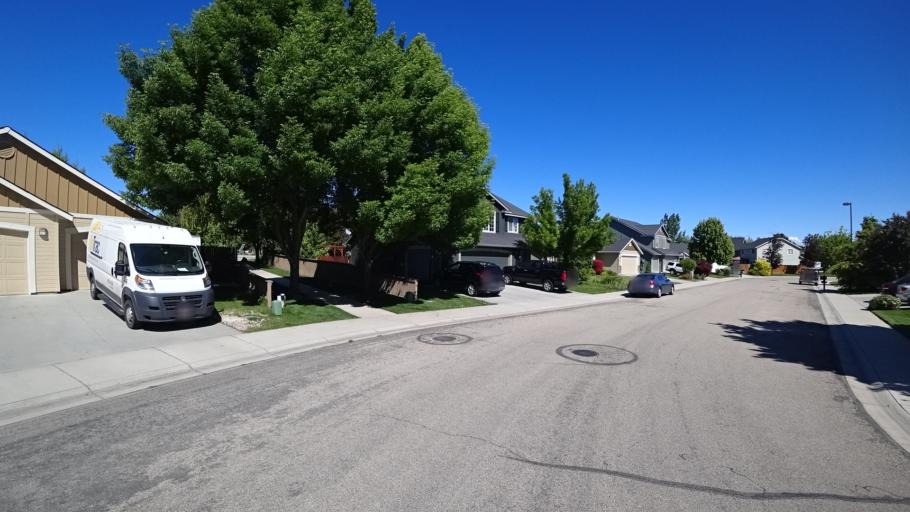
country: US
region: Idaho
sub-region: Ada County
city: Meridian
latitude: 43.6357
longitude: -116.3928
